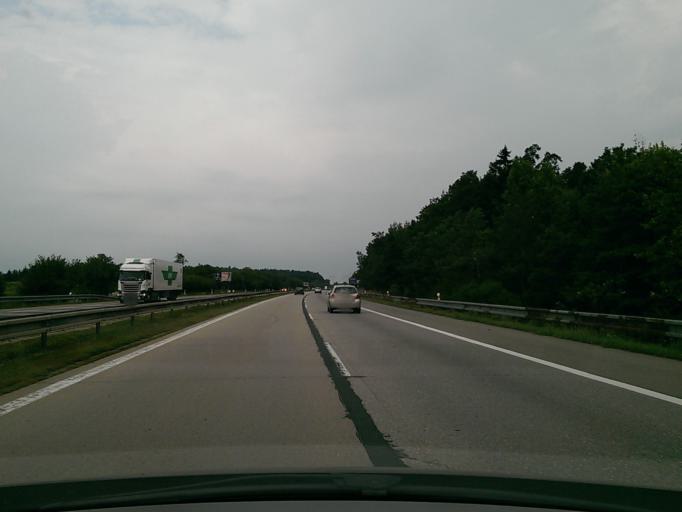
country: CZ
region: South Moravian
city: Ricany
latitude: 49.2361
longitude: 16.3754
